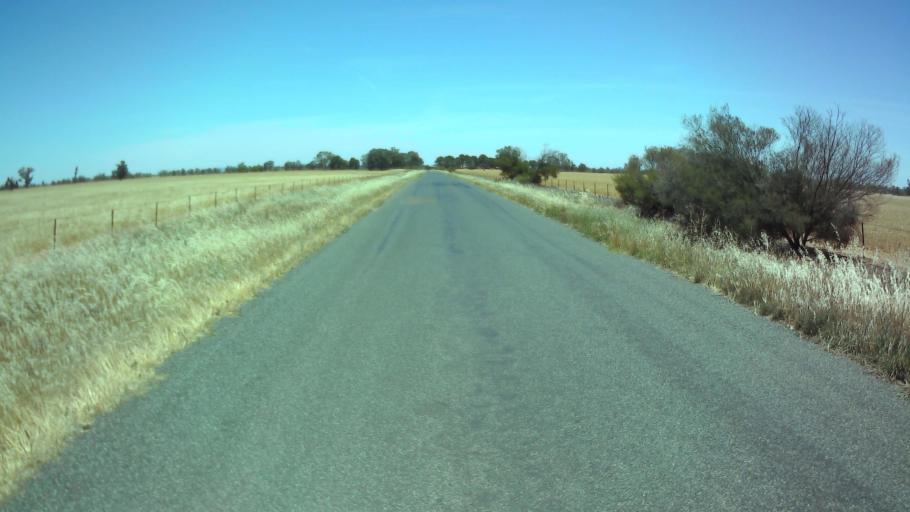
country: AU
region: New South Wales
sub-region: Weddin
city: Grenfell
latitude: -34.0418
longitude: 147.7879
